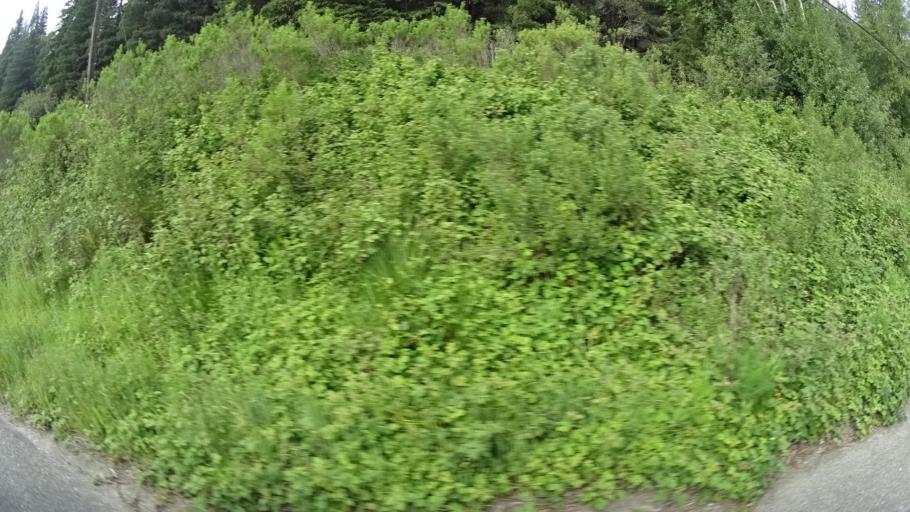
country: US
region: California
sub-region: Humboldt County
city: Redway
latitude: 40.2300
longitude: -123.8302
